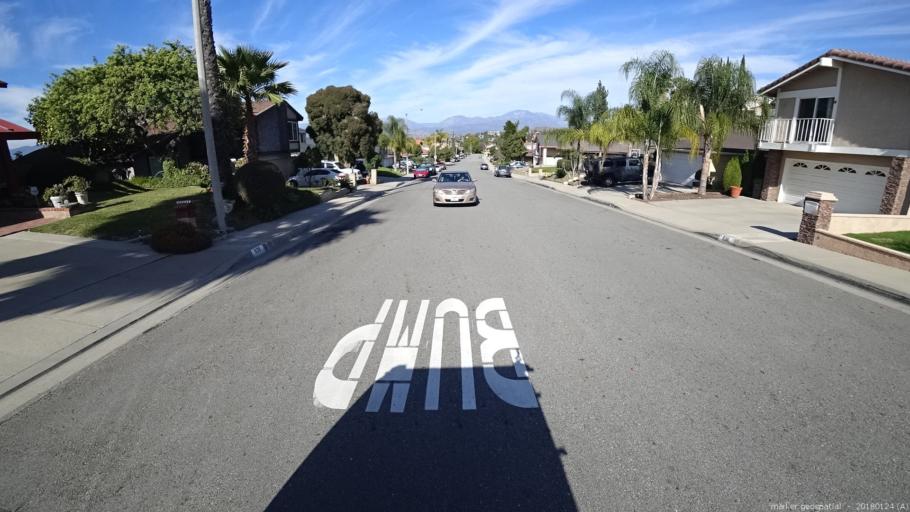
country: US
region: California
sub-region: Los Angeles County
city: Diamond Bar
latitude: 34.0128
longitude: -117.8124
